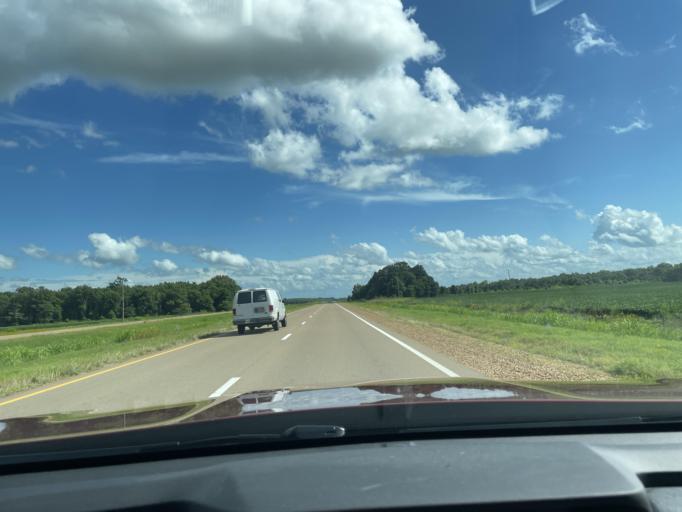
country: US
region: Mississippi
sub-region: Humphreys County
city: Belzoni
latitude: 33.0411
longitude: -90.4673
